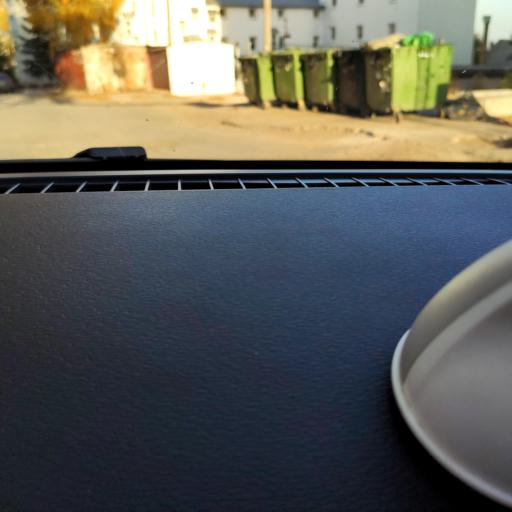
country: RU
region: Samara
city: Samara
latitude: 53.1946
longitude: 50.2108
